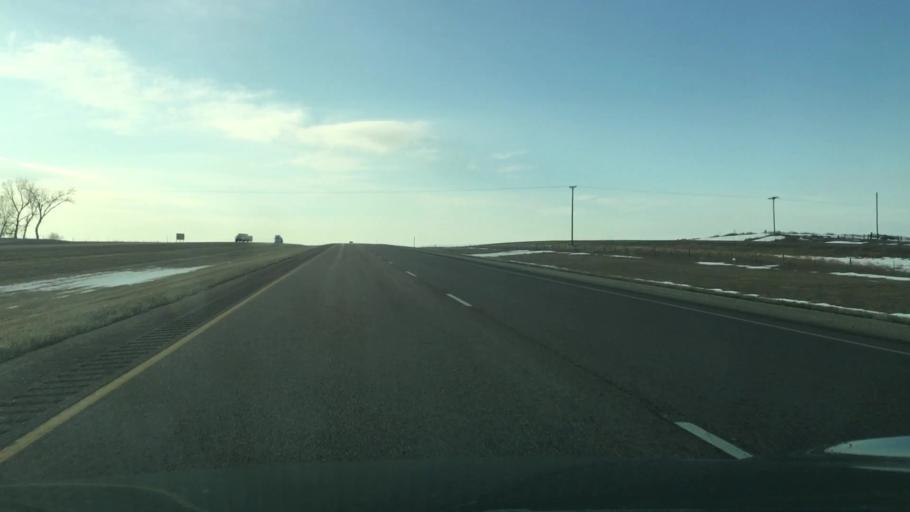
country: US
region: South Dakota
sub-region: Lyman County
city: Kennebec
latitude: 43.8965
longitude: -99.8863
